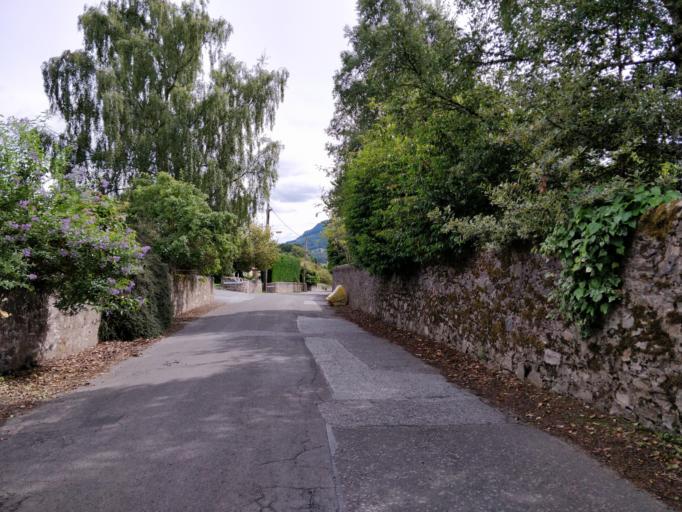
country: GB
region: Scotland
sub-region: Perth and Kinross
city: Pitlochry
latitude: 56.7062
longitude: -3.7292
